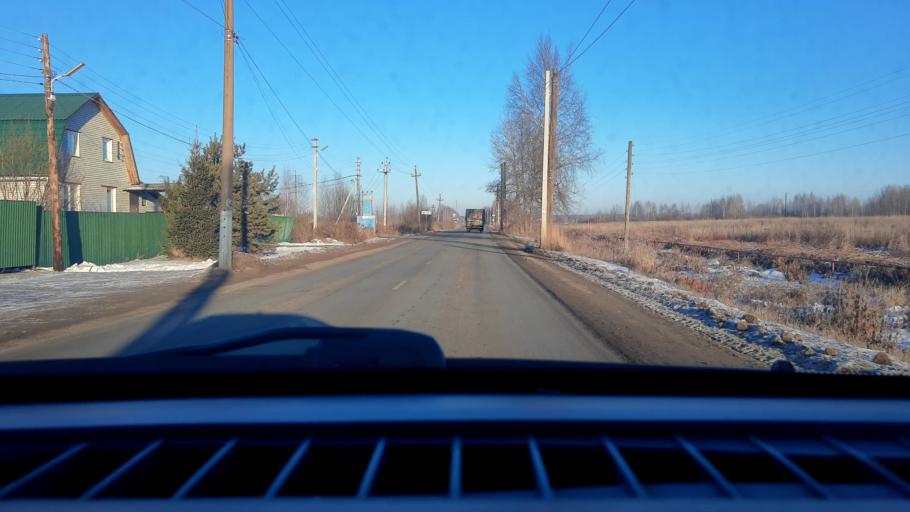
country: RU
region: Nizjnij Novgorod
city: Bor
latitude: 56.3807
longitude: 44.0804
